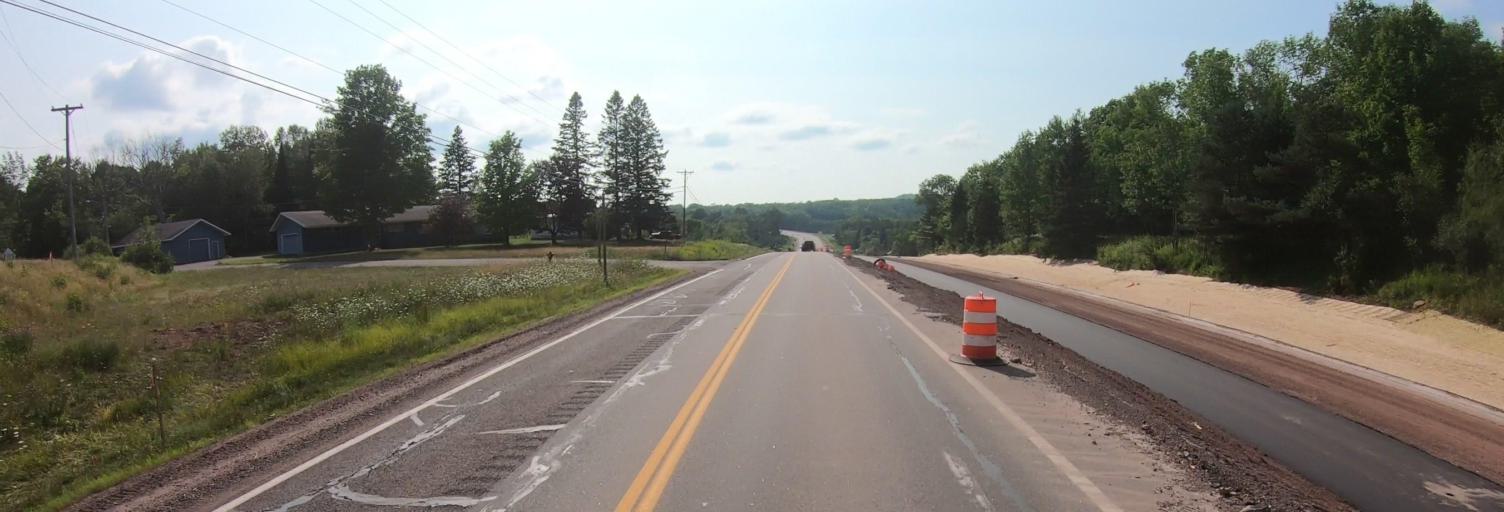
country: US
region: Michigan
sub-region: Gogebic County
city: Bessemer
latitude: 46.4812
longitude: -90.0725
